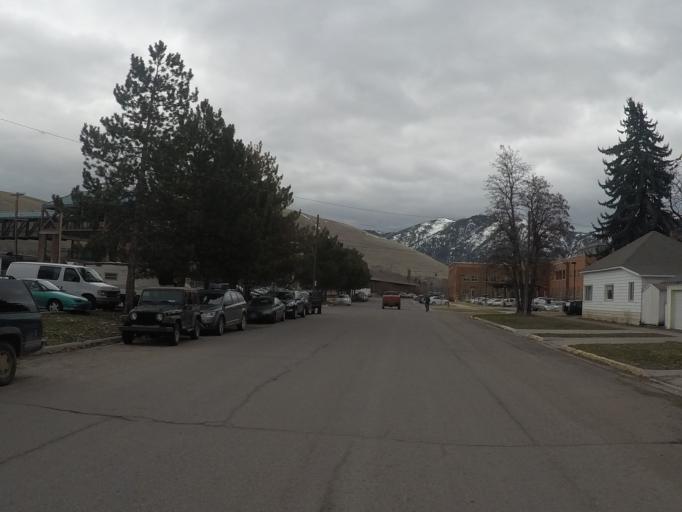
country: US
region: Montana
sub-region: Missoula County
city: Missoula
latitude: 46.8780
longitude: -113.9982
